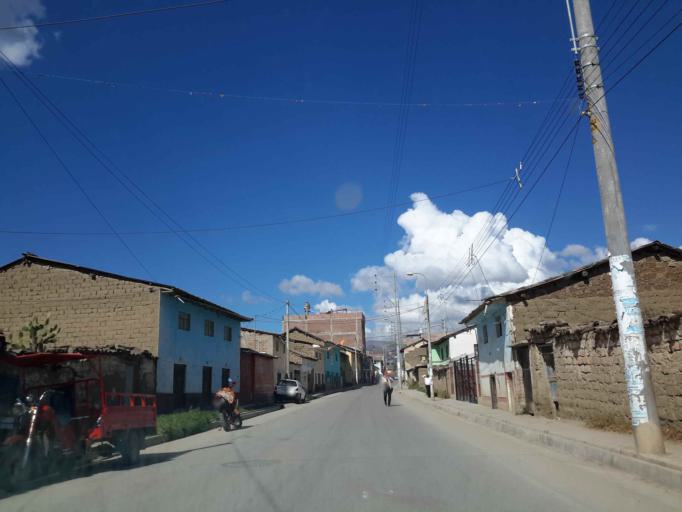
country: PE
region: Apurimac
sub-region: Provincia de Andahuaylas
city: Talavera
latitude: -13.6530
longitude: -73.4322
